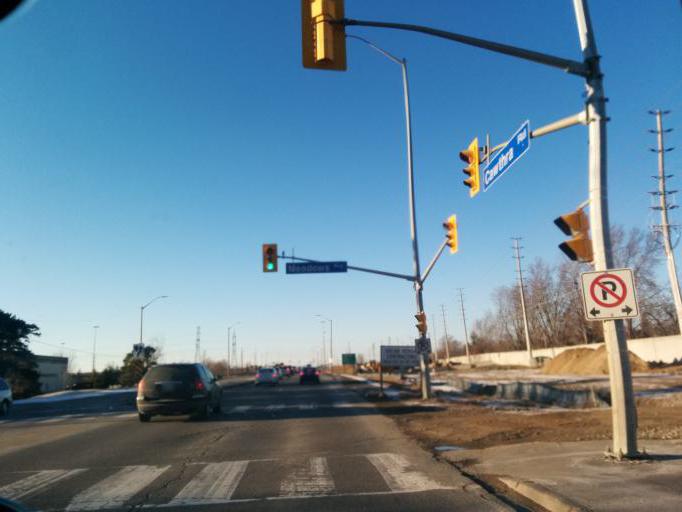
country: CA
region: Ontario
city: Mississauga
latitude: 43.6130
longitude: -79.6251
